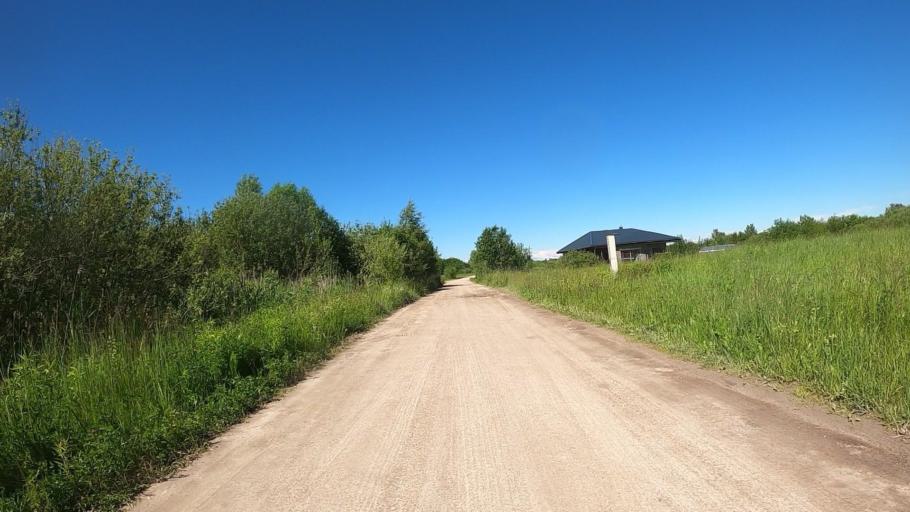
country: LV
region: Salaspils
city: Salaspils
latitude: 56.8424
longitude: 24.3988
